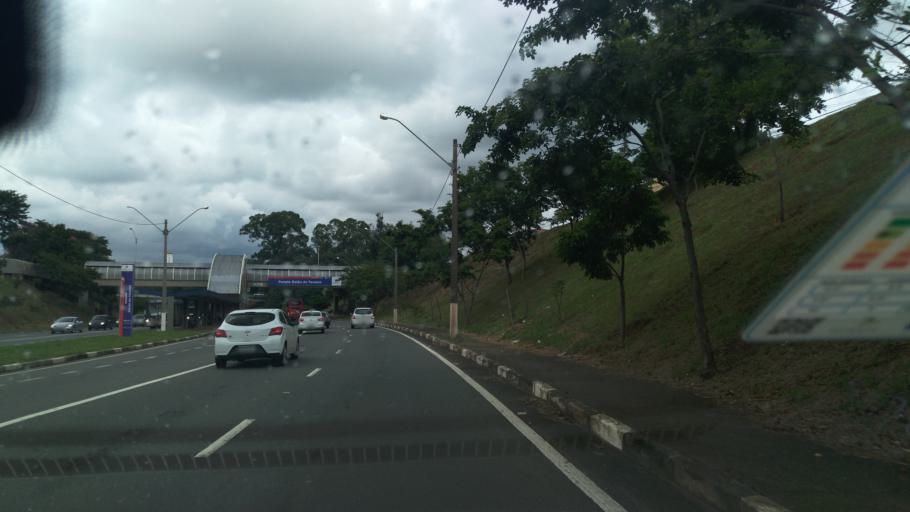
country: BR
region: Sao Paulo
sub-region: Campinas
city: Campinas
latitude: -22.8971
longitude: -47.0948
